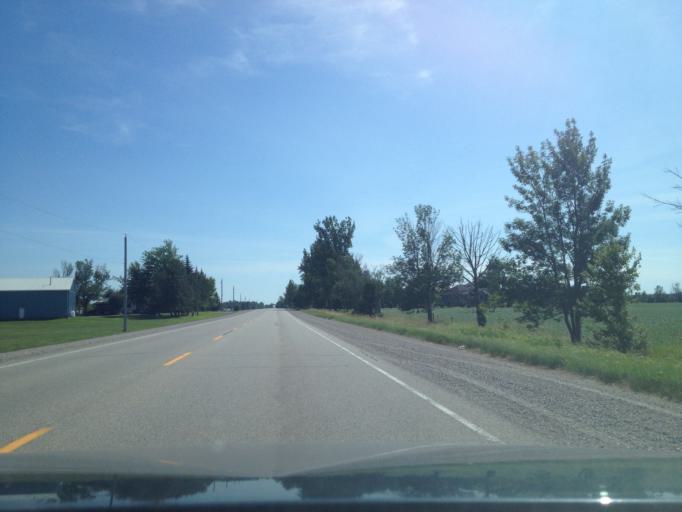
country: CA
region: Ontario
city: Stratford
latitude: 43.4902
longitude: -80.8863
